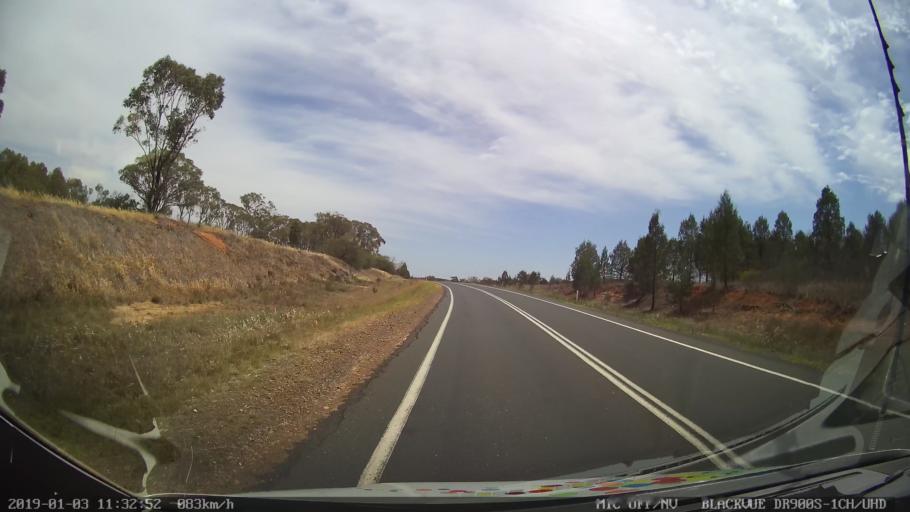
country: AU
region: New South Wales
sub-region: Weddin
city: Grenfell
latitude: -33.9530
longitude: 148.1762
